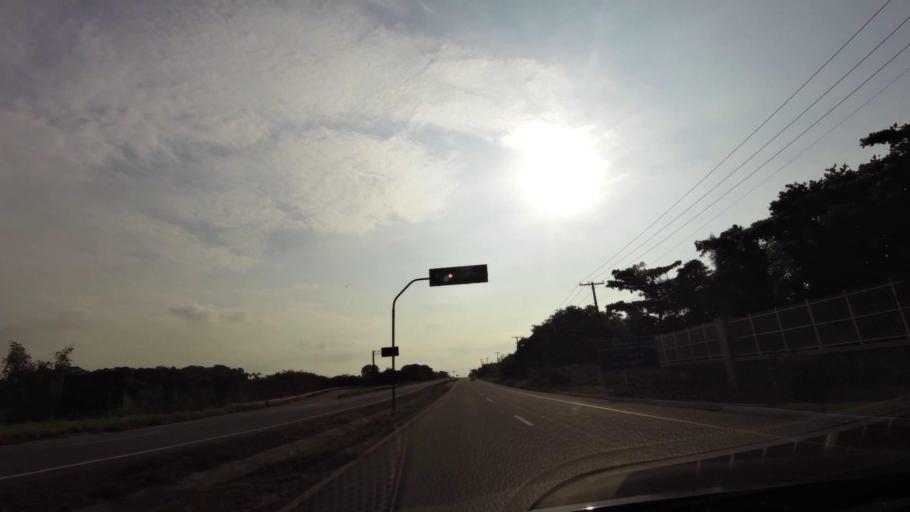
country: BR
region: Espirito Santo
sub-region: Guarapari
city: Guarapari
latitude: -20.5272
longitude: -40.3792
